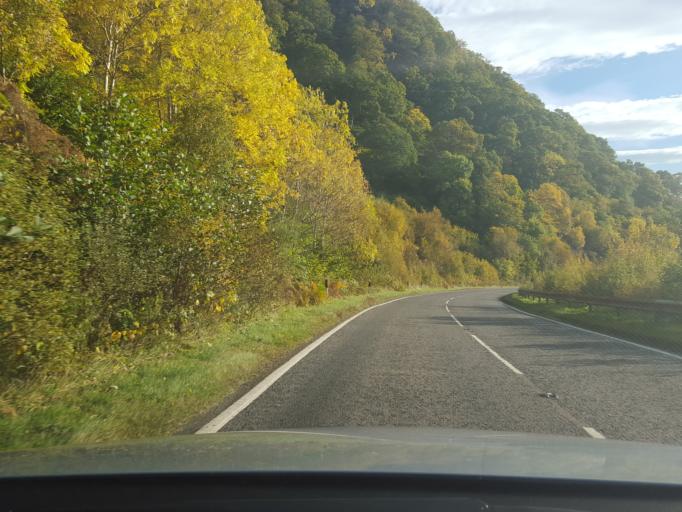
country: GB
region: Scotland
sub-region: Highland
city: Fort William
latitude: 57.2616
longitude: -5.4955
